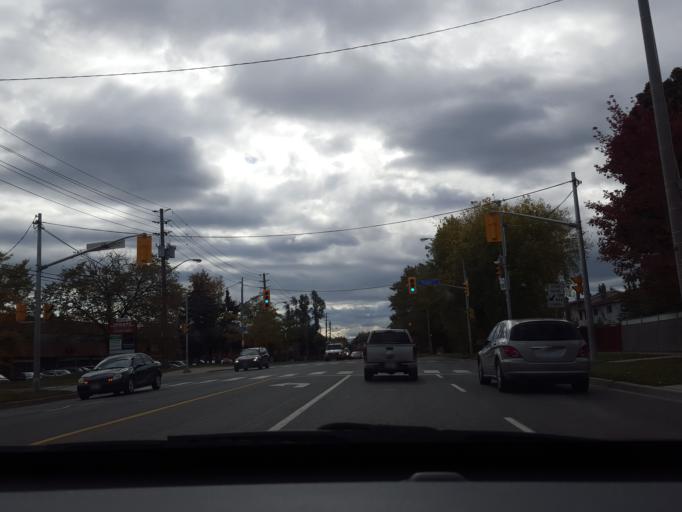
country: CA
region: Ontario
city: Scarborough
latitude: 43.8042
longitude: -79.2985
